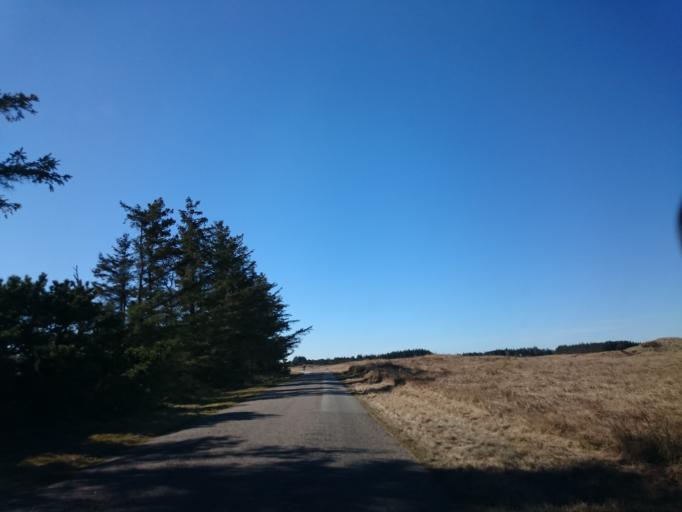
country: DK
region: North Denmark
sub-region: Frederikshavn Kommune
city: Strandby
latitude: 57.6256
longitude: 10.3505
